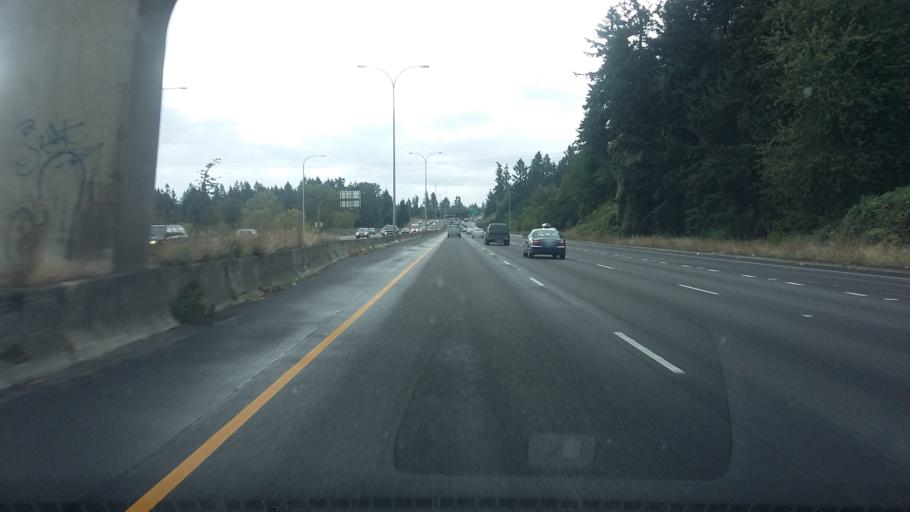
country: US
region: Washington
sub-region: Clark County
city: Hazel Dell
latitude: 45.6567
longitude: -122.6644
